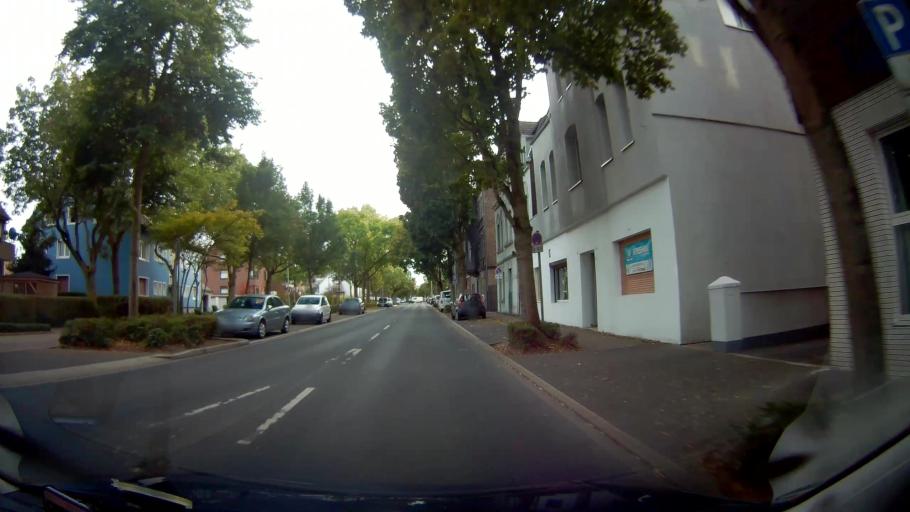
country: DE
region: North Rhine-Westphalia
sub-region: Regierungsbezirk Arnsberg
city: Herne
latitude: 51.5470
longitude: 7.2616
